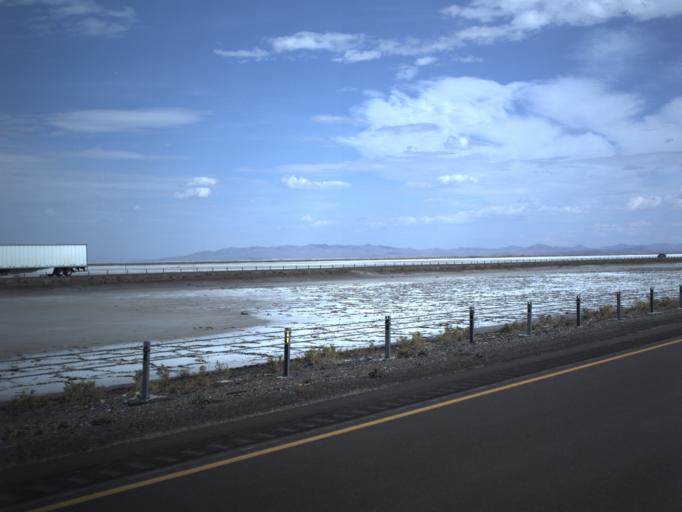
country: US
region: Utah
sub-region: Tooele County
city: Wendover
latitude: 40.7290
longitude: -113.4207
